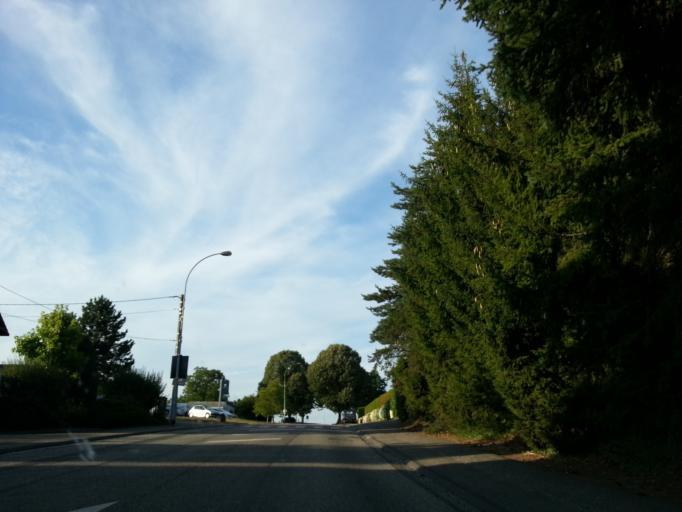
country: FR
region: Alsace
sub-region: Departement du Bas-Rhin
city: Soultz-sous-Forets
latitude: 48.9403
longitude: 7.8850
